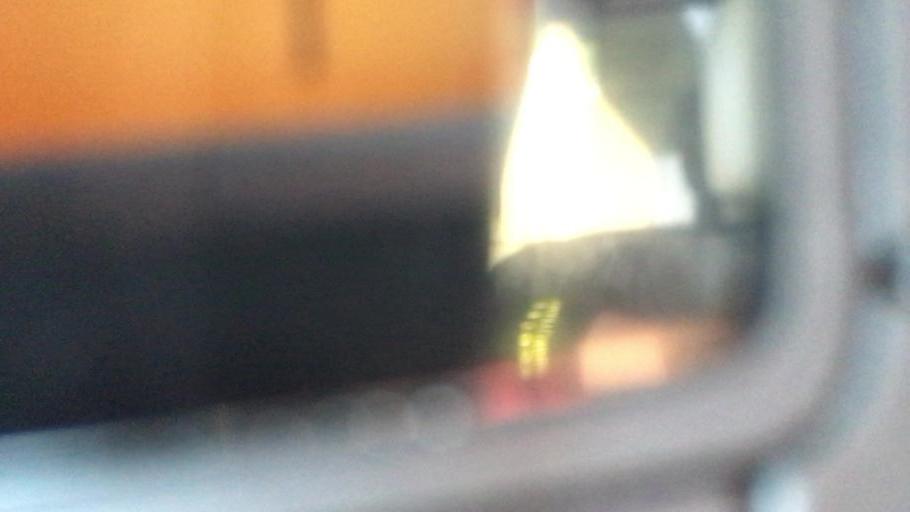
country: US
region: Maryland
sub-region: Worcester County
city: Pocomoke City
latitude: 38.0952
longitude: -75.6206
